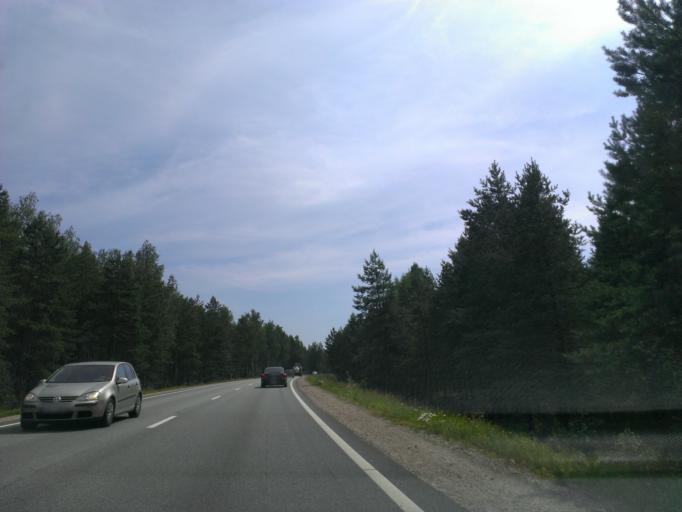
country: LV
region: Riga
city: Bergi
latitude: 56.9645
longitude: 24.3684
